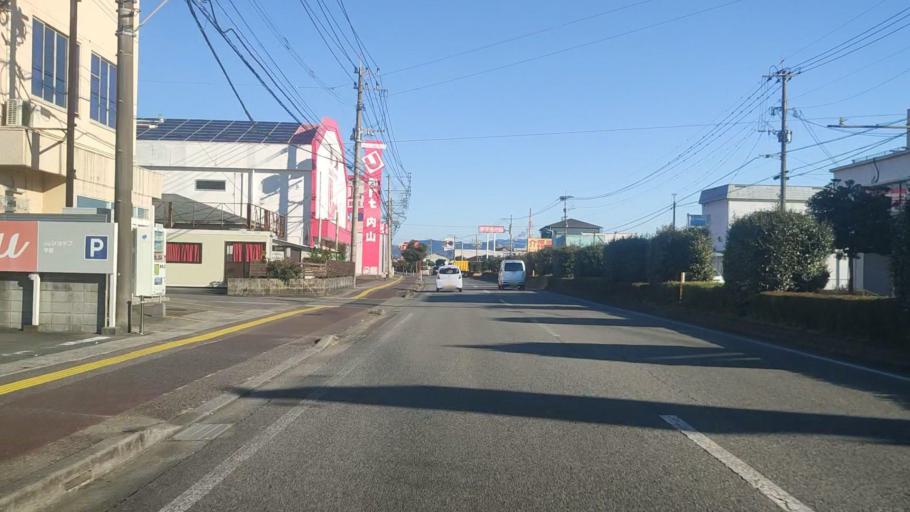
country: JP
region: Miyazaki
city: Nobeoka
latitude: 32.5531
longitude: 131.6787
